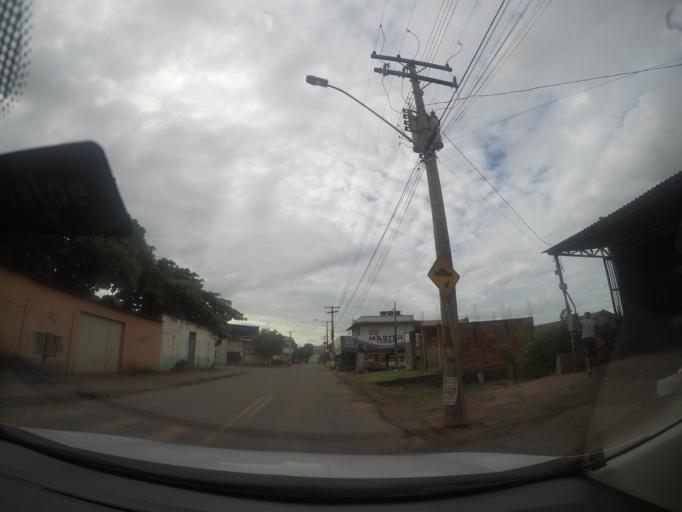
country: BR
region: Goias
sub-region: Goiania
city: Goiania
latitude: -16.6198
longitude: -49.3289
